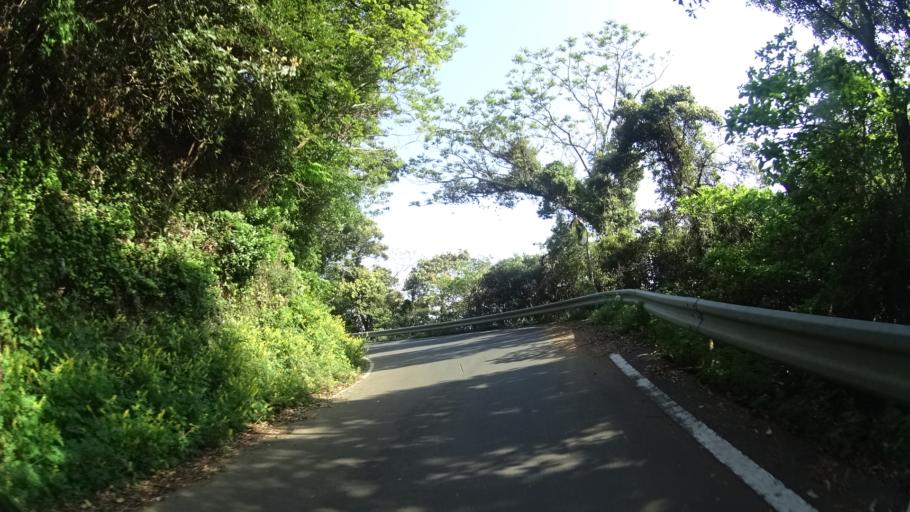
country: JP
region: Oita
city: Tsukumiura
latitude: 33.3569
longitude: 132.0358
